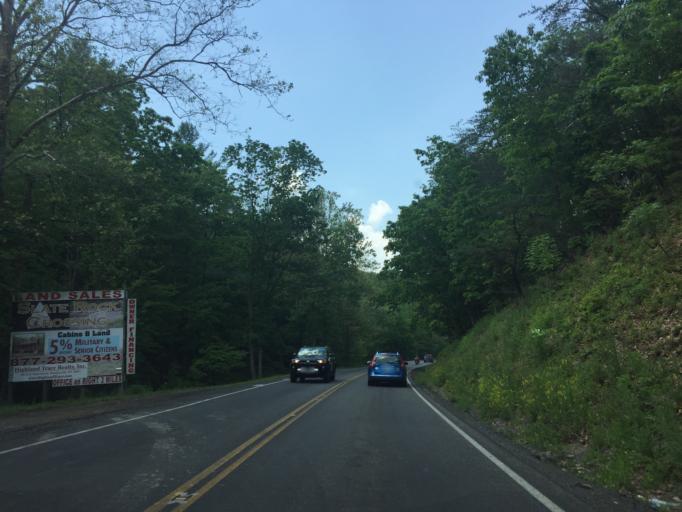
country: US
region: Virginia
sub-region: Shenandoah County
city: Woodstock
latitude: 39.0884
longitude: -78.5534
